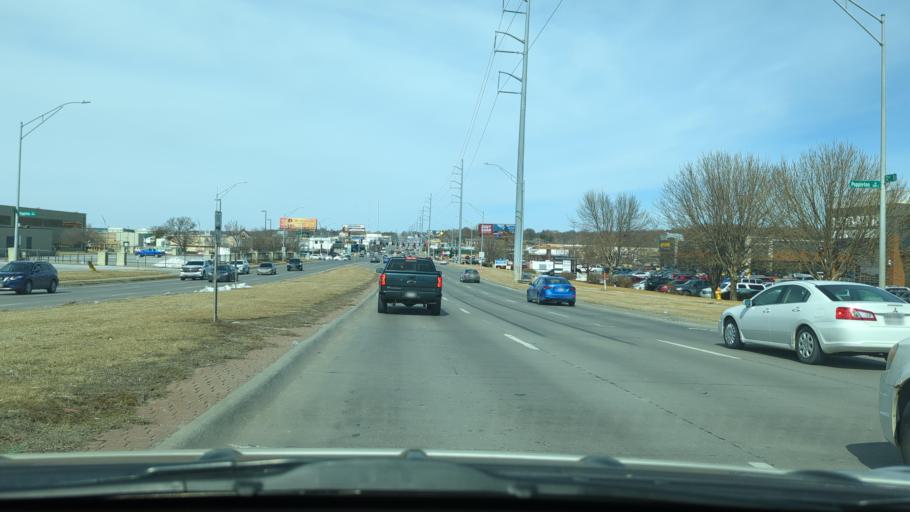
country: US
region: Nebraska
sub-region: Douglas County
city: Ralston
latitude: 41.2465
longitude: -96.0239
